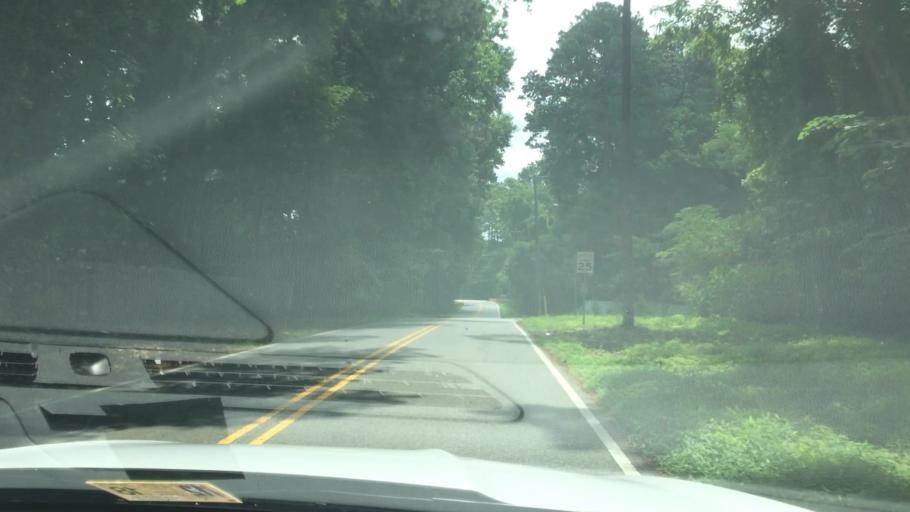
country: US
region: Virginia
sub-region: City of Poquoson
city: Poquoson
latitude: 37.1385
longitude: -76.4552
